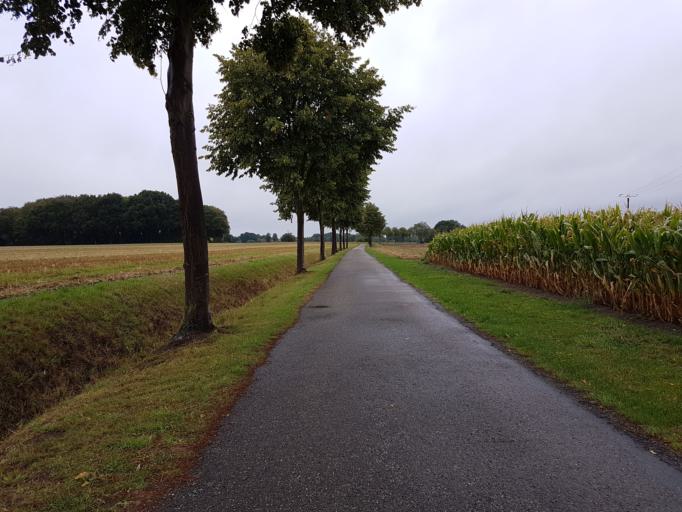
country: DE
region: North Rhine-Westphalia
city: Olfen
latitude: 51.7174
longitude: 7.3971
